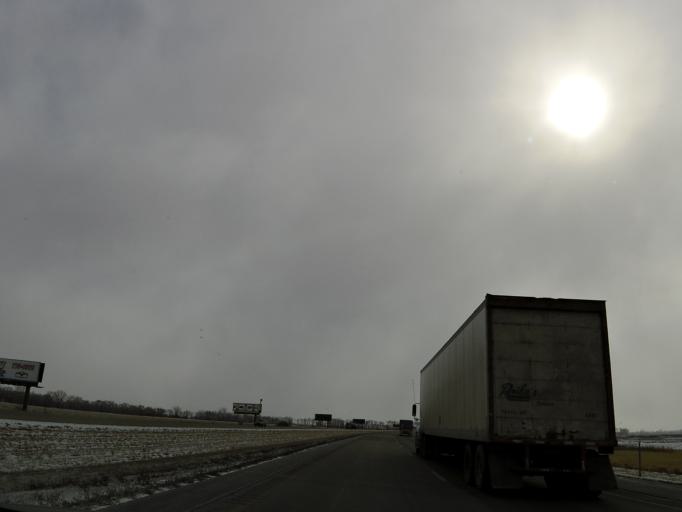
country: US
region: North Dakota
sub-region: Grand Forks County
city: Grand Forks
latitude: 47.8384
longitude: -97.0783
